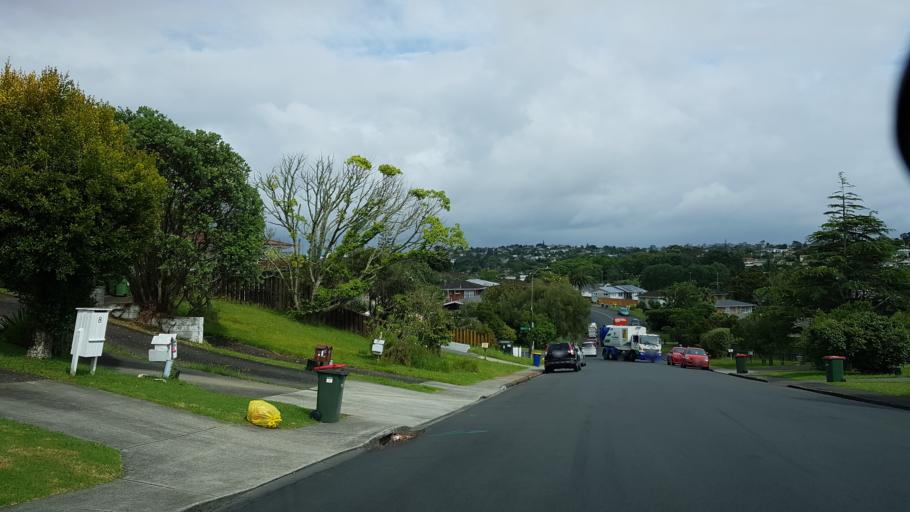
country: NZ
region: Auckland
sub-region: Auckland
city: North Shore
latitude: -36.7877
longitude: 174.7385
